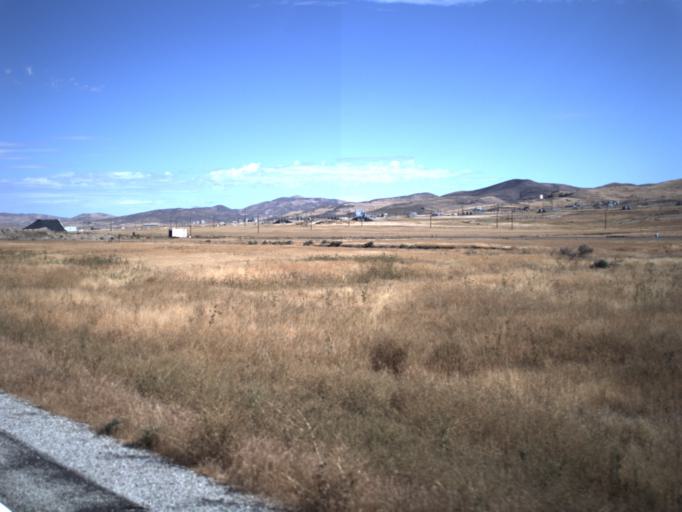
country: US
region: Utah
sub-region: Box Elder County
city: Tremonton
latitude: 41.6912
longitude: -112.4439
